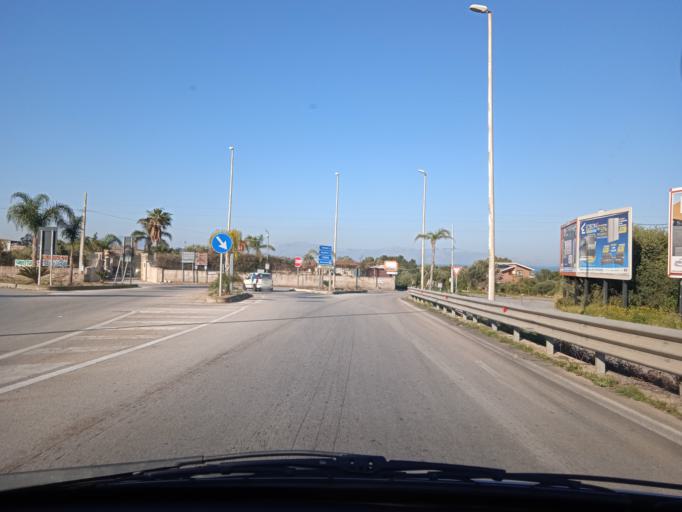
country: IT
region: Sicily
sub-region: Palermo
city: Cinisi
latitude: 38.1733
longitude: 13.1094
